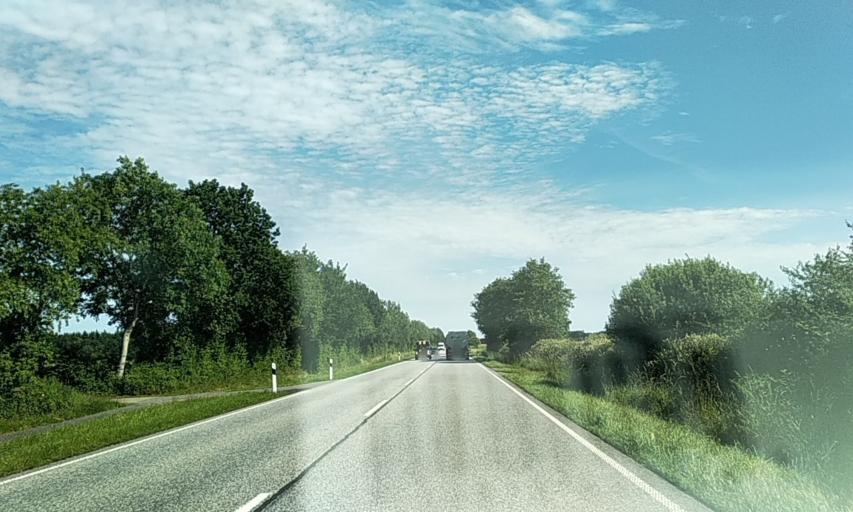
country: DE
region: Schleswig-Holstein
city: Kropp
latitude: 54.4225
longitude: 9.5307
